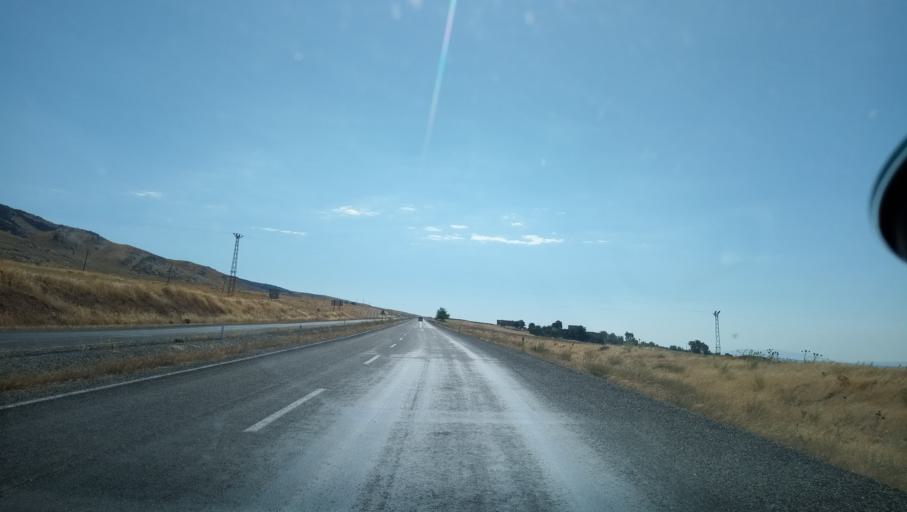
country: TR
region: Diyarbakir
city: Silvan
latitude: 38.1280
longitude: 41.0579
